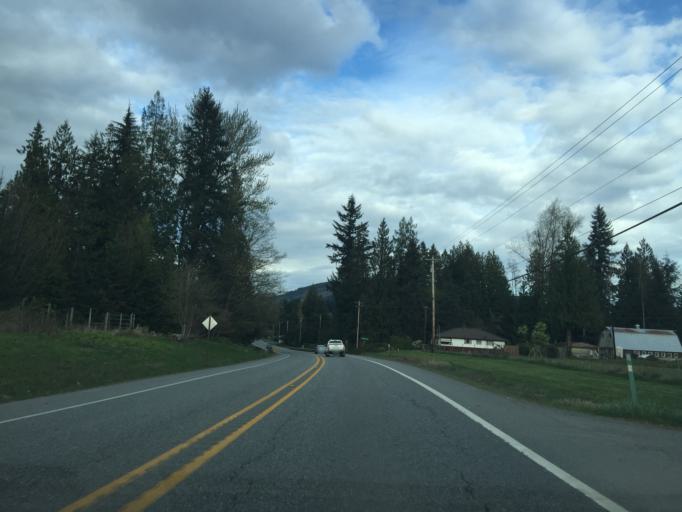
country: US
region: Washington
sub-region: Snohomish County
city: Arlington Heights
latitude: 48.2260
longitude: -122.0936
